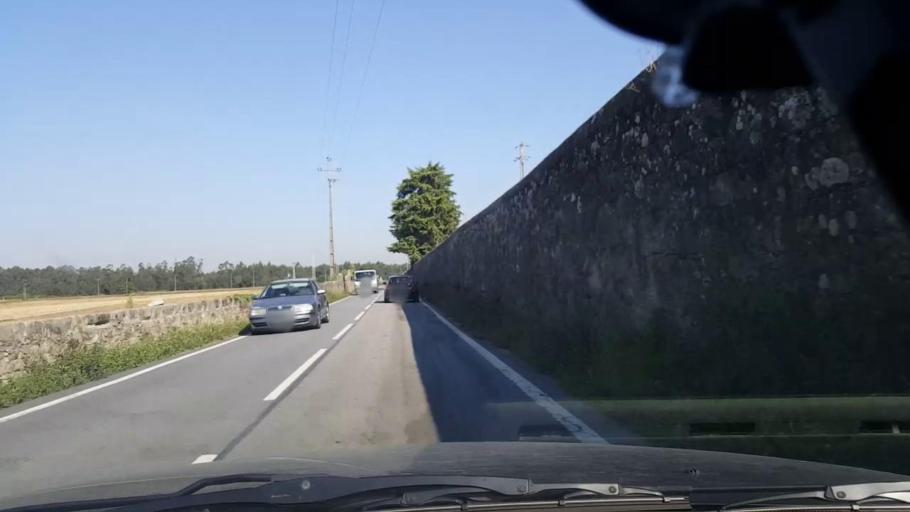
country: PT
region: Porto
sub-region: Vila do Conde
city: Arvore
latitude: 41.3233
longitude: -8.6807
